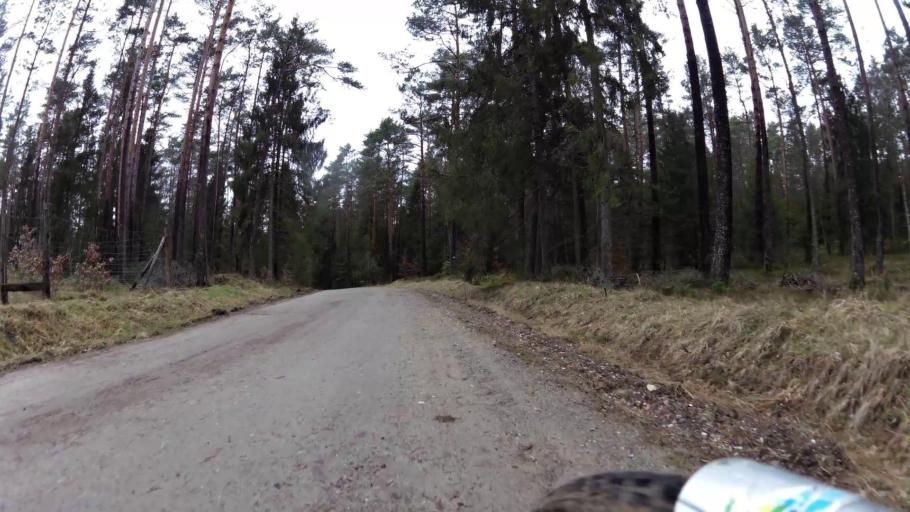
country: PL
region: Pomeranian Voivodeship
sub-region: Powiat bytowski
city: Borzytuchom
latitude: 54.2642
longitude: 17.3510
